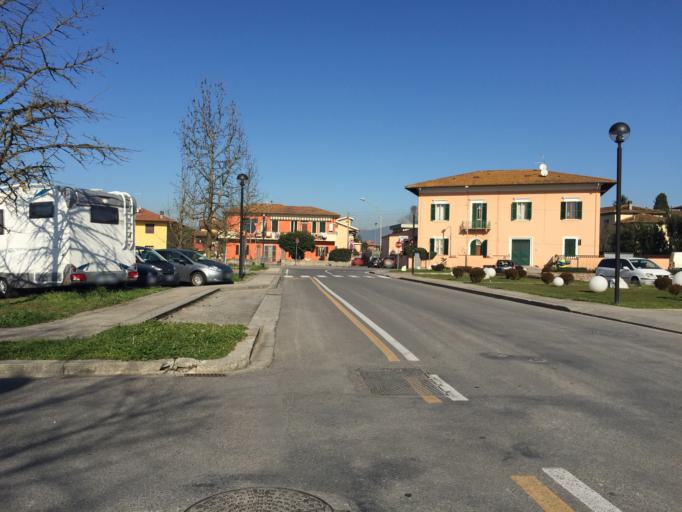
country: IT
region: Tuscany
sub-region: Provincia di Pistoia
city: Ponte Buggianese
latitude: 43.8392
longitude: 10.7461
